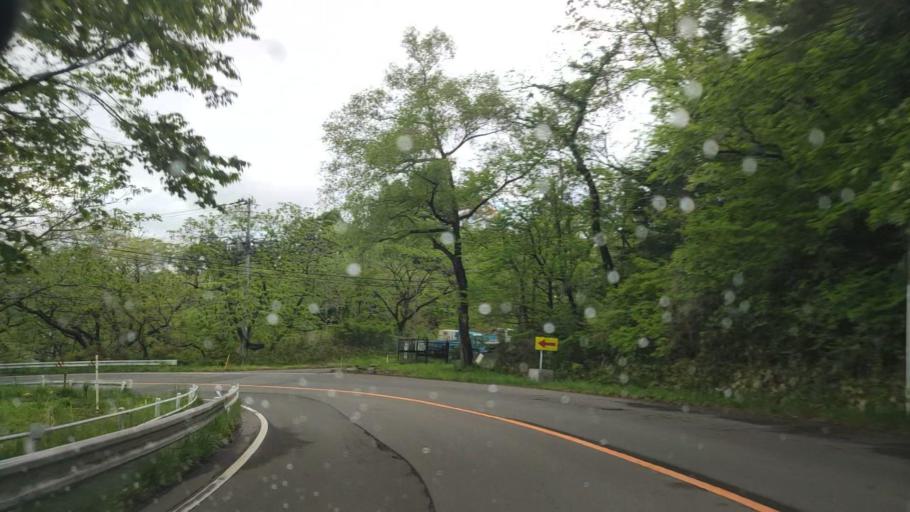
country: JP
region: Miyagi
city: Sendai
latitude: 38.2570
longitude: 140.8486
